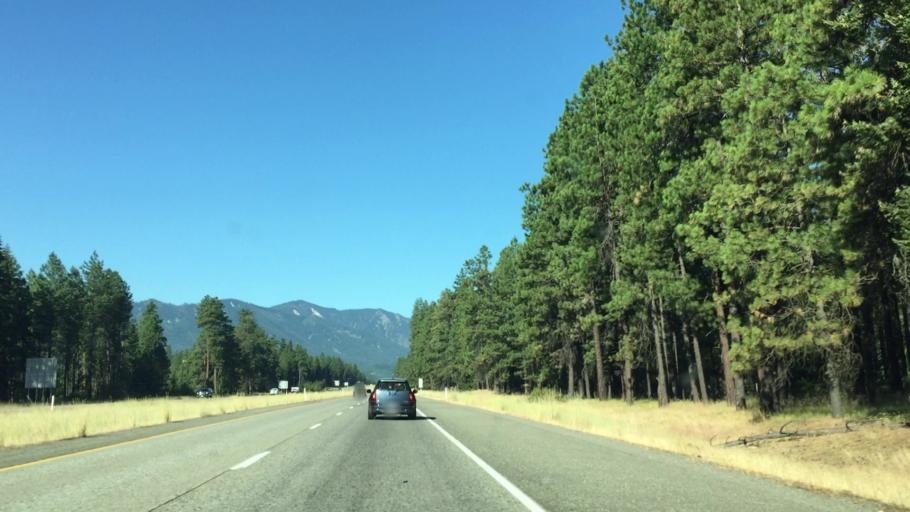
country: US
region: Washington
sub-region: Kittitas County
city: Cle Elum
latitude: 47.1933
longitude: -120.9680
